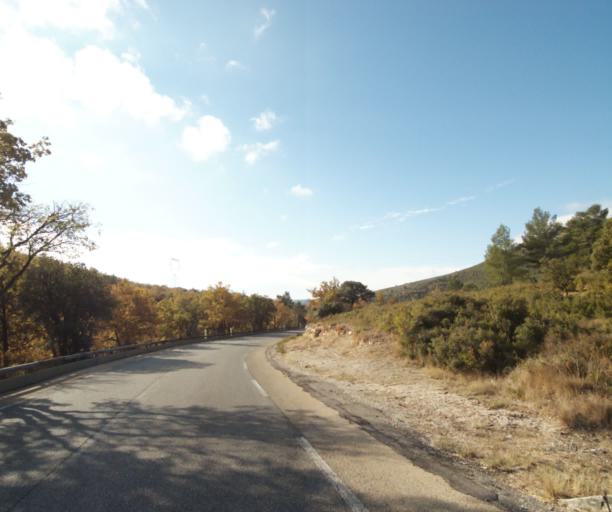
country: FR
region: Provence-Alpes-Cote d'Azur
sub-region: Departement des Bouches-du-Rhone
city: Cadolive
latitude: 43.3809
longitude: 5.5441
